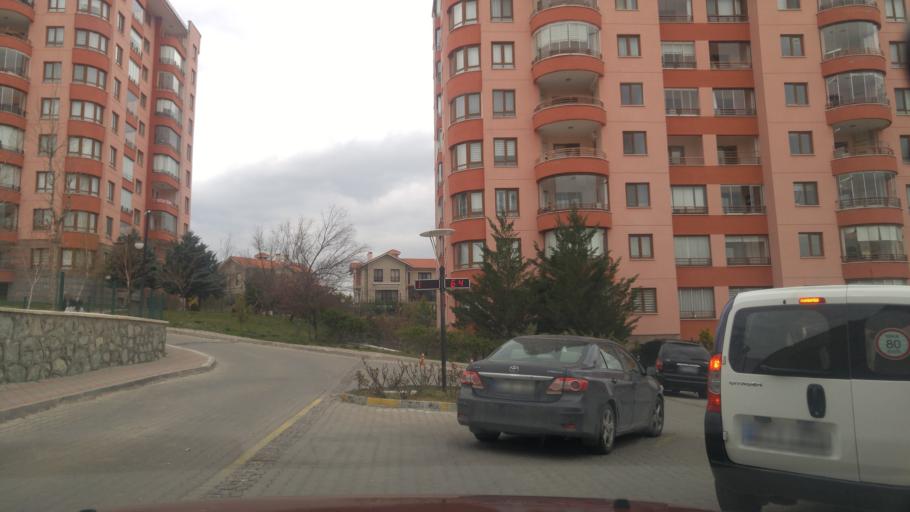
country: TR
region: Ankara
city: Etimesgut
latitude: 39.8604
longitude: 32.6733
